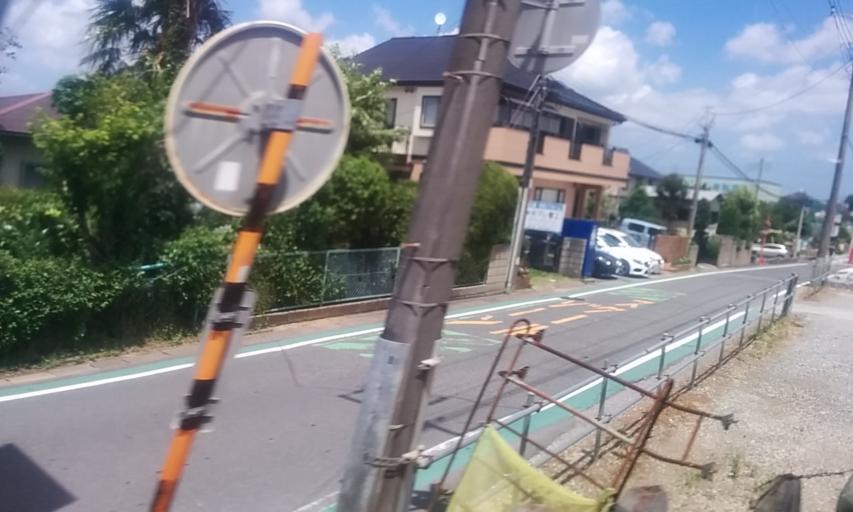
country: JP
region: Chiba
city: Chiba
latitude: 35.5478
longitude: 140.2108
